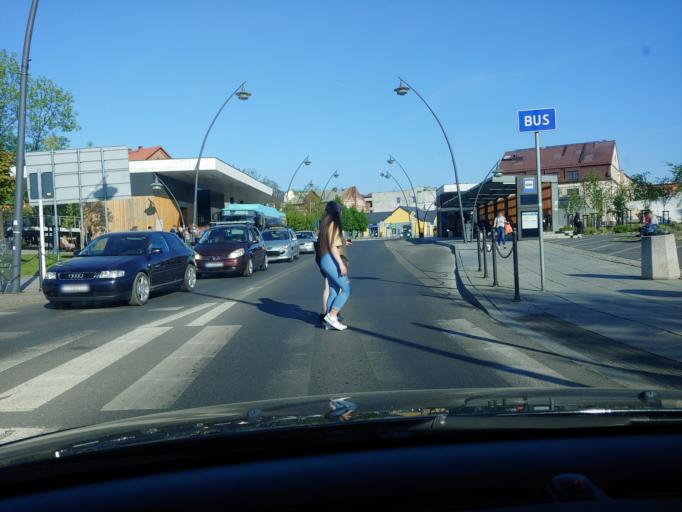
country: PL
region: Silesian Voivodeship
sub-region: Jaworzno
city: Jaworzno
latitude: 50.2035
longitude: 19.2704
